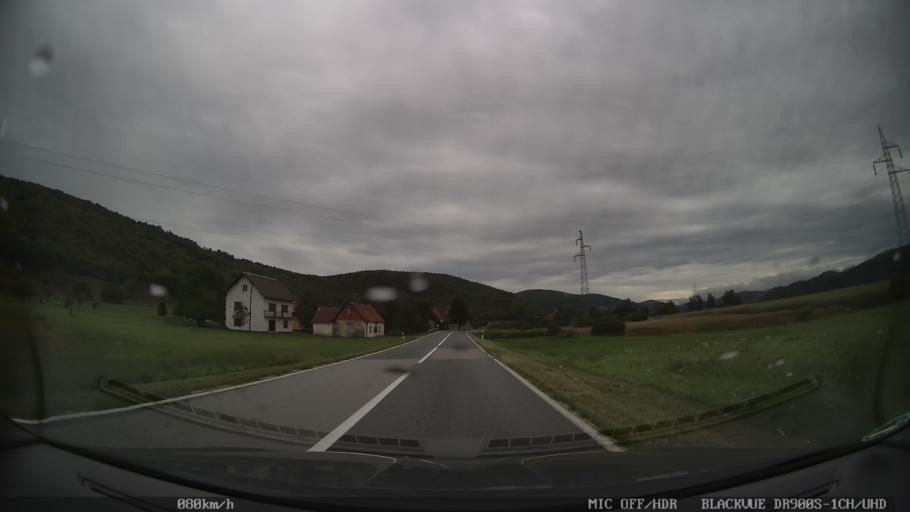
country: HR
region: Licko-Senjska
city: Brinje
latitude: 44.9191
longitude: 15.1501
